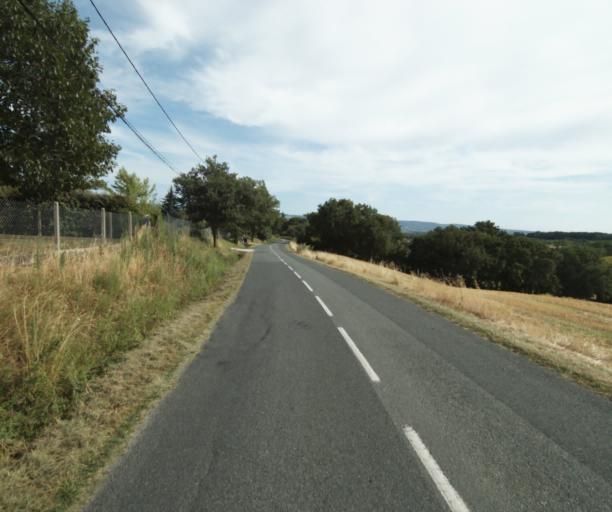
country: FR
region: Midi-Pyrenees
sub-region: Departement du Tarn
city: Puylaurens
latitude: 43.5408
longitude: 2.0593
